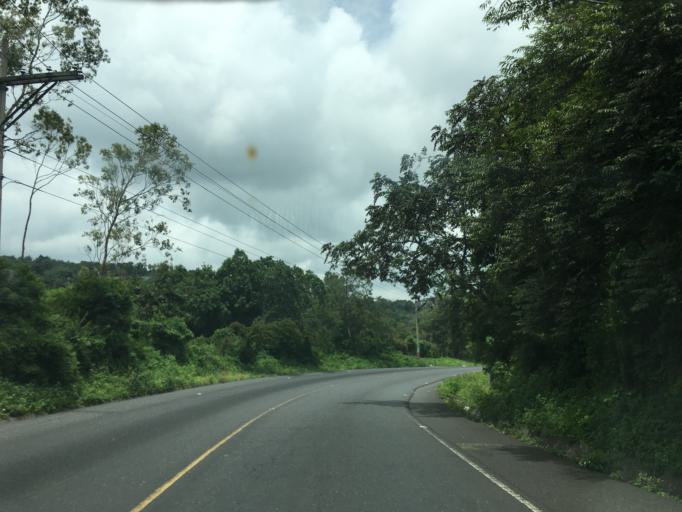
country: GT
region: Sacatepequez
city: Alotenango
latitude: 14.4530
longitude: -90.8112
